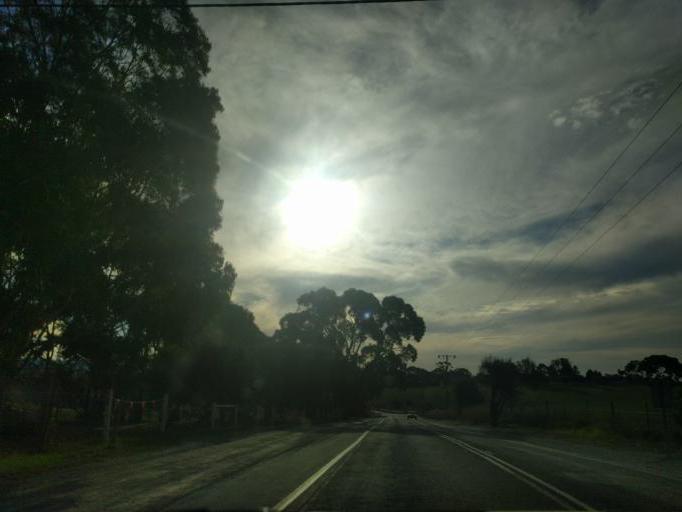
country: AU
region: South Australia
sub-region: Mount Barker
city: Little Hampton
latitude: -35.0456
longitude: 138.8346
